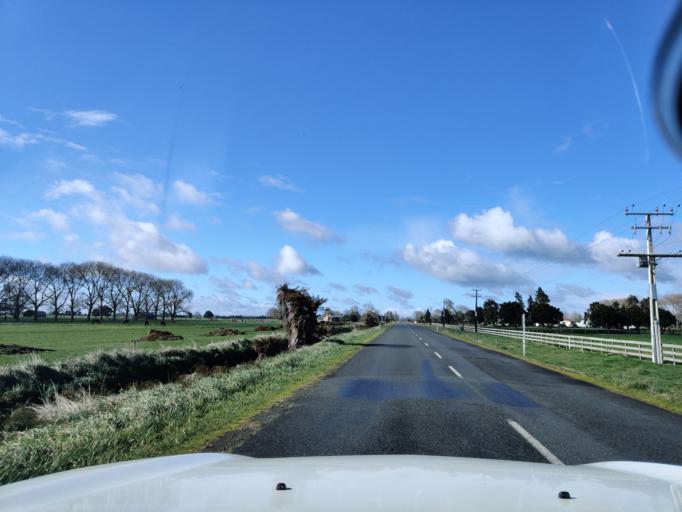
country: NZ
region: Waikato
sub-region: Waikato District
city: Ngaruawahia
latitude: -37.5916
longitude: 175.2915
